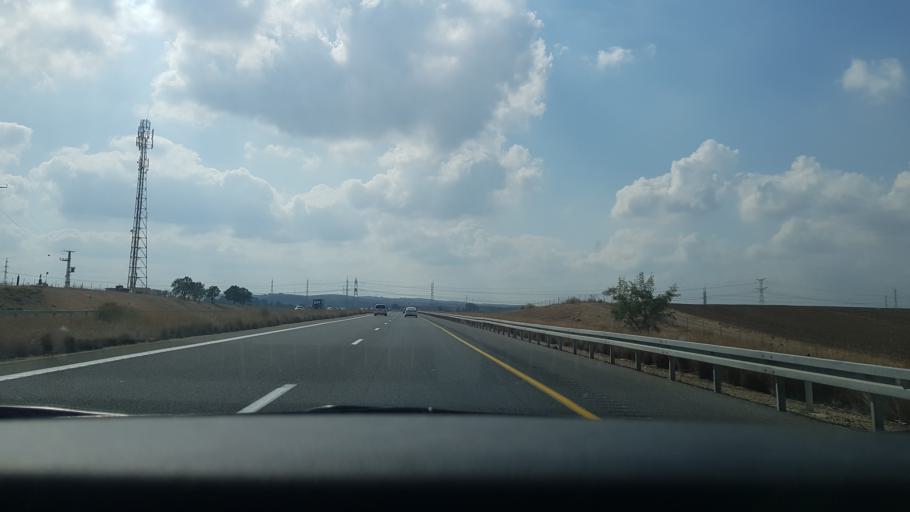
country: IL
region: Central District
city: Bene 'Ayish
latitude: 31.7190
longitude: 34.8204
